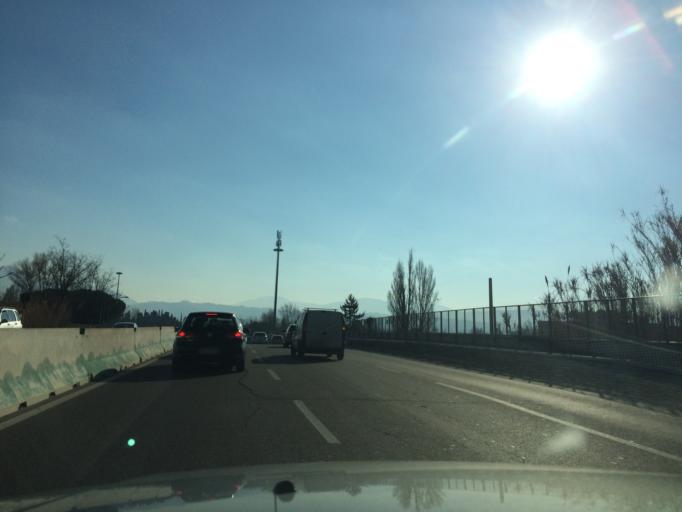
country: IT
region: Umbria
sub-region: Provincia di Terni
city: Terni
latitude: 42.5704
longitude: 12.6304
